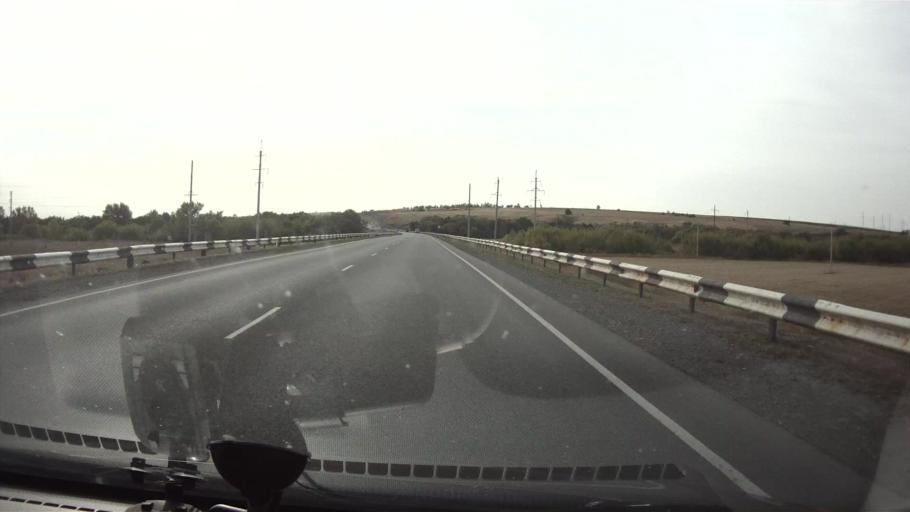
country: RU
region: Saratov
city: Sennoy
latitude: 52.1432
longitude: 46.8965
